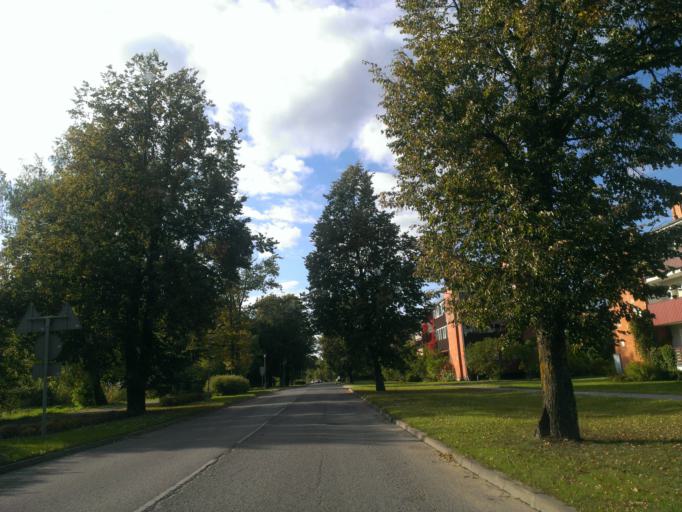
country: LV
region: Sigulda
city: Sigulda
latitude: 57.1595
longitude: 24.8642
